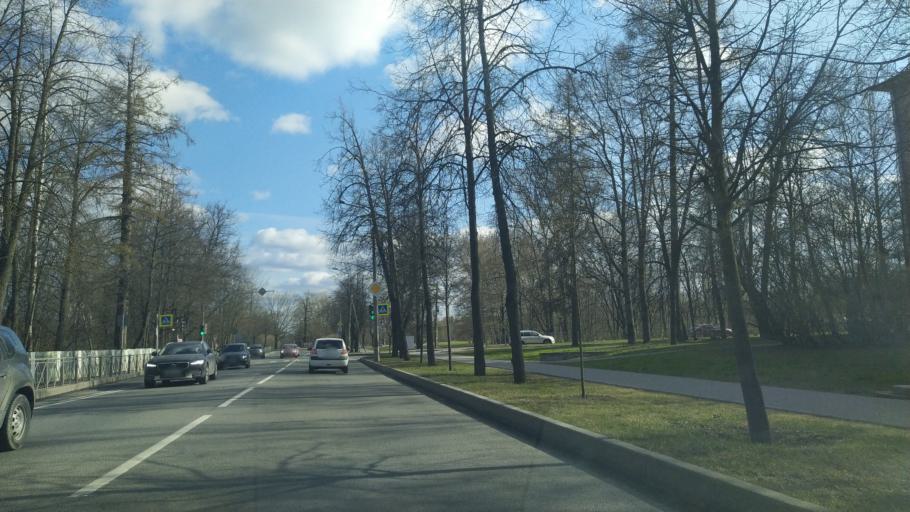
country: RU
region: St.-Petersburg
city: Pushkin
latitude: 59.7043
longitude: 30.4188
